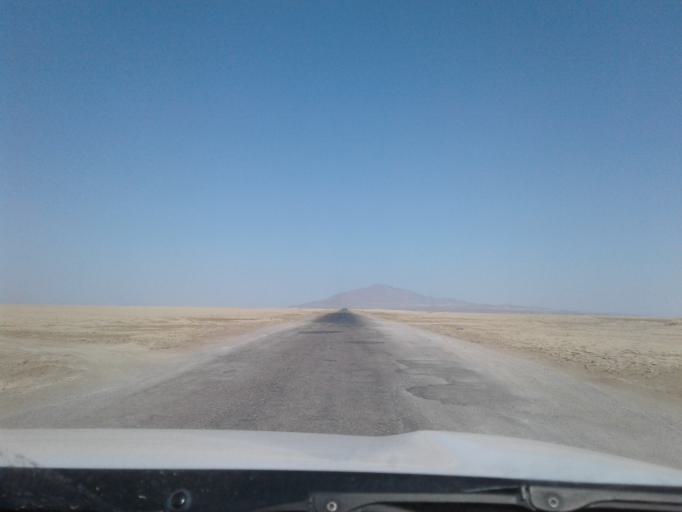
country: TM
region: Balkan
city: Gumdag
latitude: 39.2124
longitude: 54.6376
